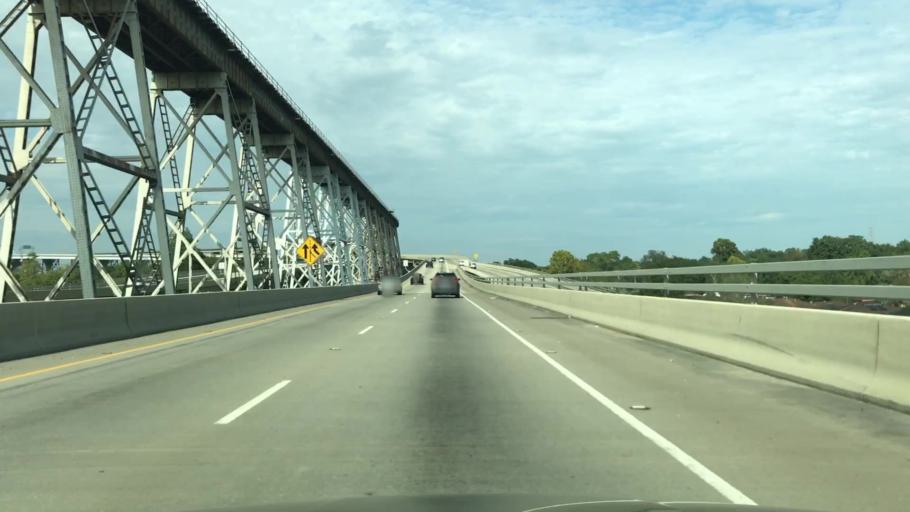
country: US
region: Louisiana
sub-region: Jefferson Parish
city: Bridge City
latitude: 29.9318
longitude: -90.1645
